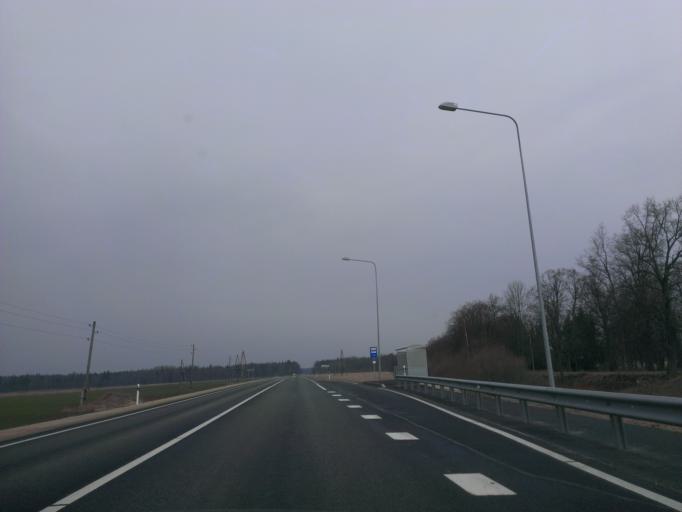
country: LV
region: Salacgrivas
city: Salacgriva
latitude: 57.7033
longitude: 24.3712
